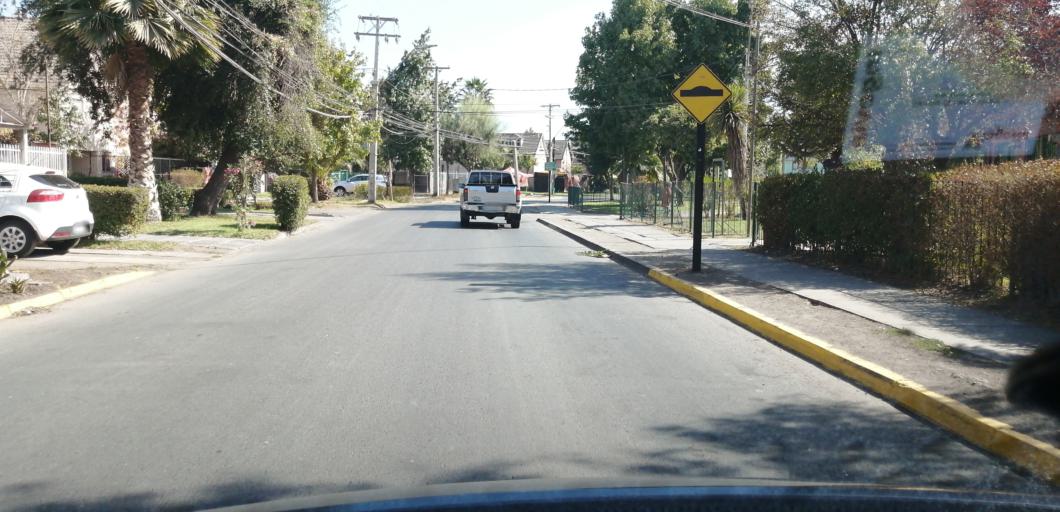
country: CL
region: Santiago Metropolitan
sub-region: Provincia de Santiago
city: Lo Prado
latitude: -33.4593
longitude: -70.7229
